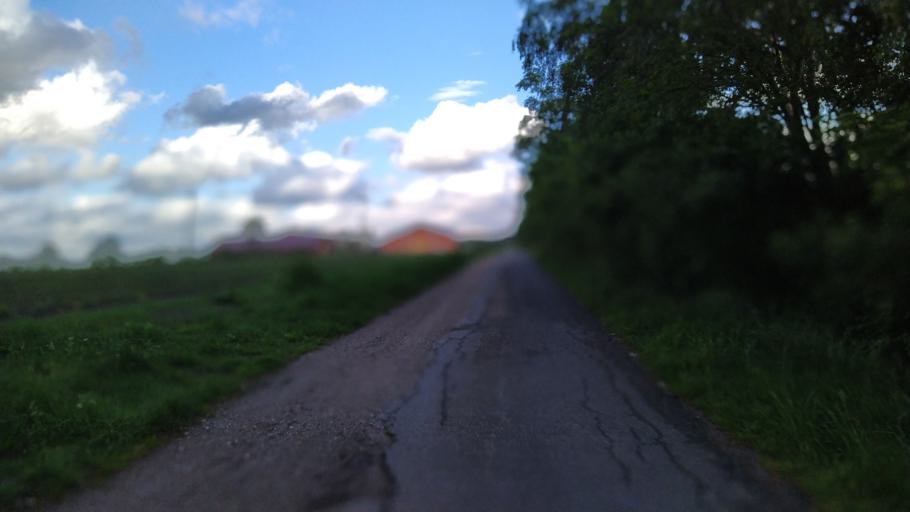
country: DE
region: Lower Saxony
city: Farven
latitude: 53.4546
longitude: 9.2882
